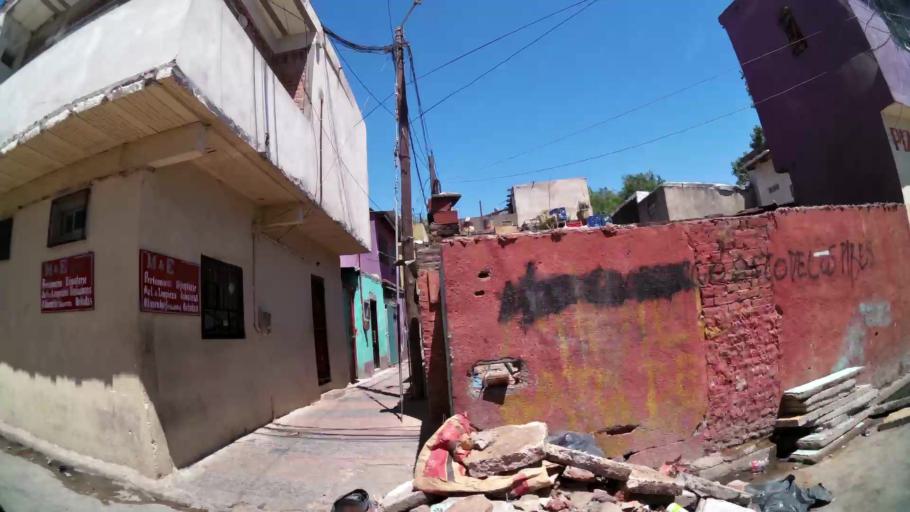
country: AR
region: Buenos Aires
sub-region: Partido de Avellaneda
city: Avellaneda
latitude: -34.6494
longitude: -58.4038
